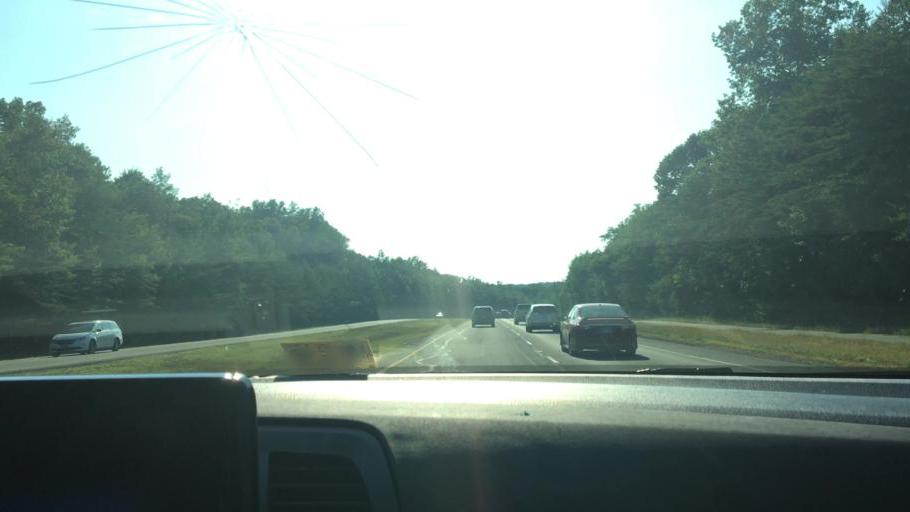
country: US
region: Virginia
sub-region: Prince William County
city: Lake Ridge
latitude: 38.6826
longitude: -77.3664
